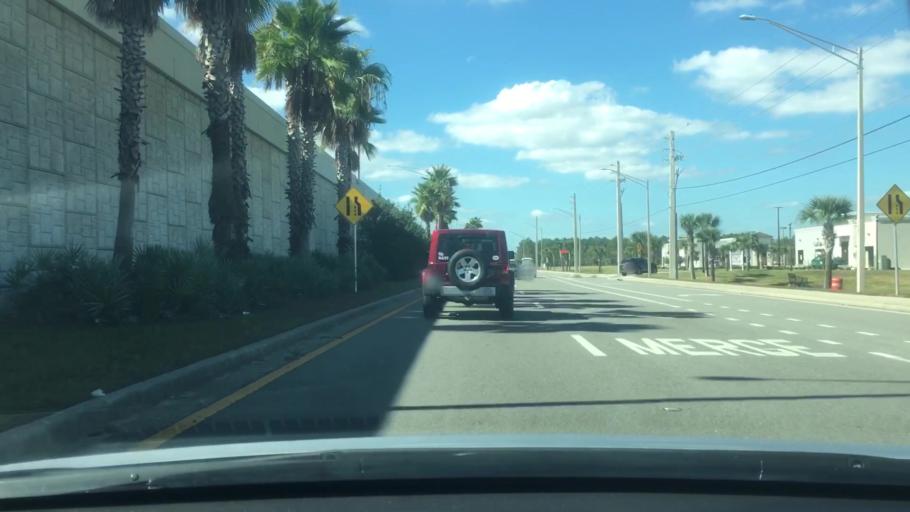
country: US
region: Florida
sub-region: Duval County
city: Atlantic Beach
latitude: 30.3201
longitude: -81.4907
